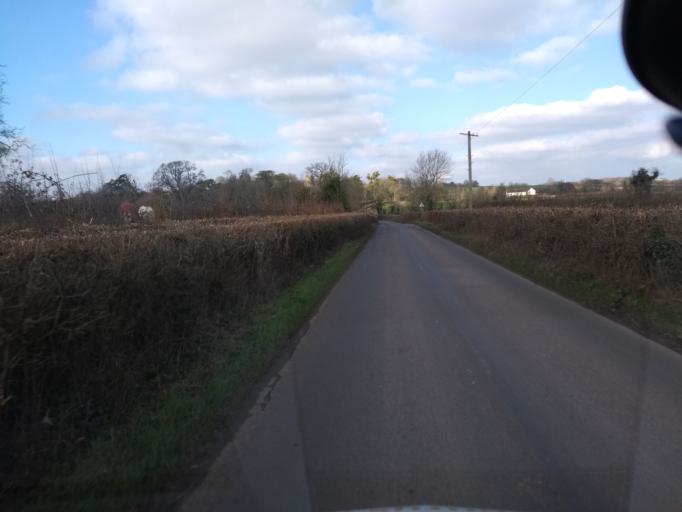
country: GB
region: England
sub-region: Somerset
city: Creech Saint Michael
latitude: 50.9557
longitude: -3.0455
